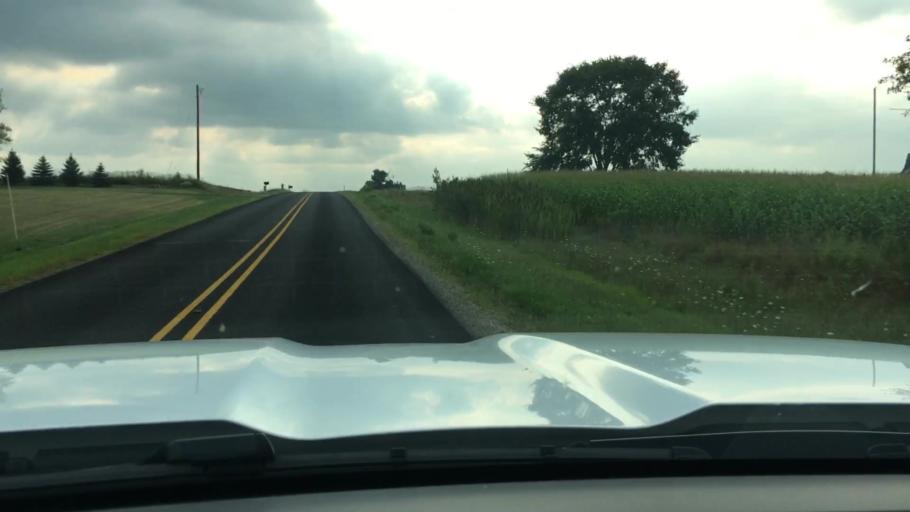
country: US
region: Michigan
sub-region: Ottawa County
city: Hudsonville
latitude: 42.8330
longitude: -85.8731
